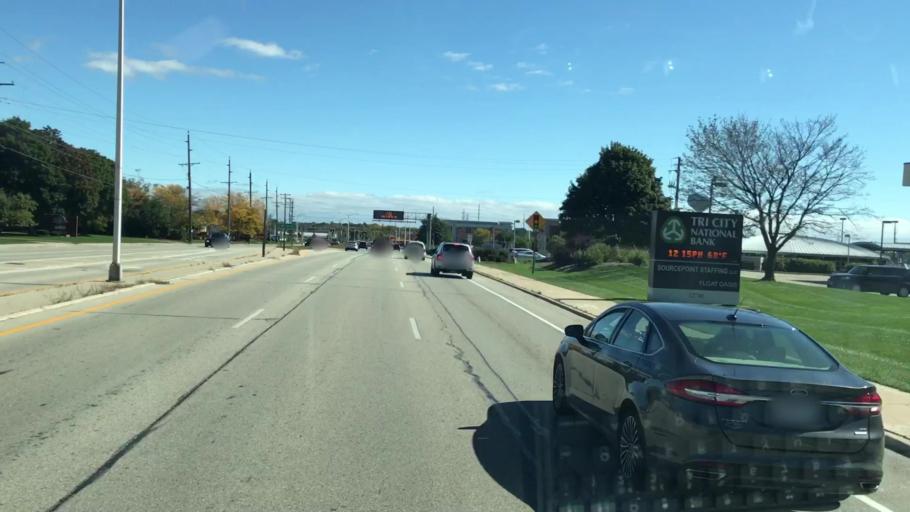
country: US
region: Wisconsin
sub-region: Waukesha County
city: Butler
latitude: 43.0890
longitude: -88.0707
